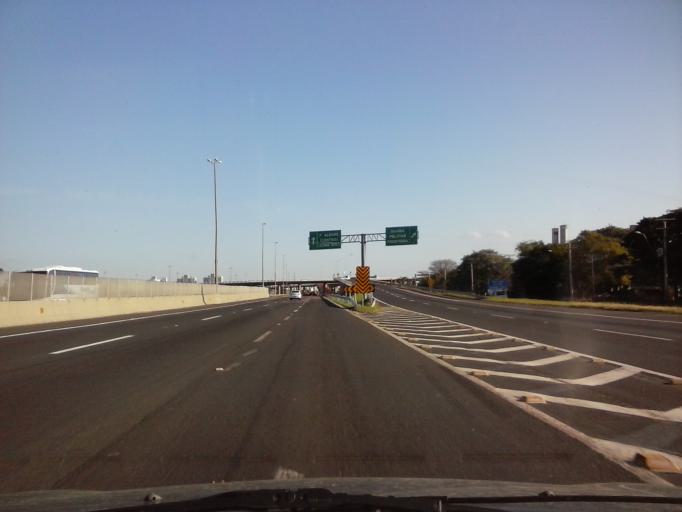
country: BR
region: Rio Grande do Sul
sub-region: Porto Alegre
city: Porto Alegre
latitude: -29.9940
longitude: -51.2054
